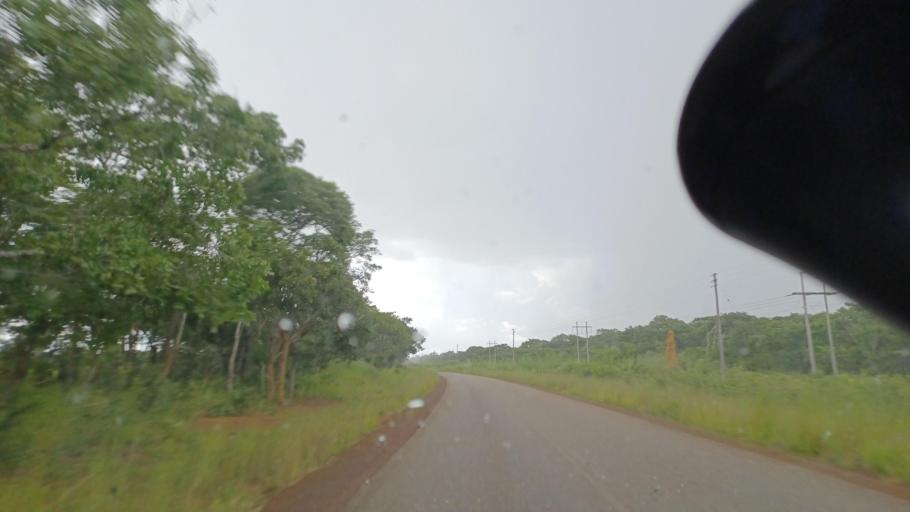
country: ZM
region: North-Western
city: Kasempa
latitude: -13.0920
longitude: 25.9256
